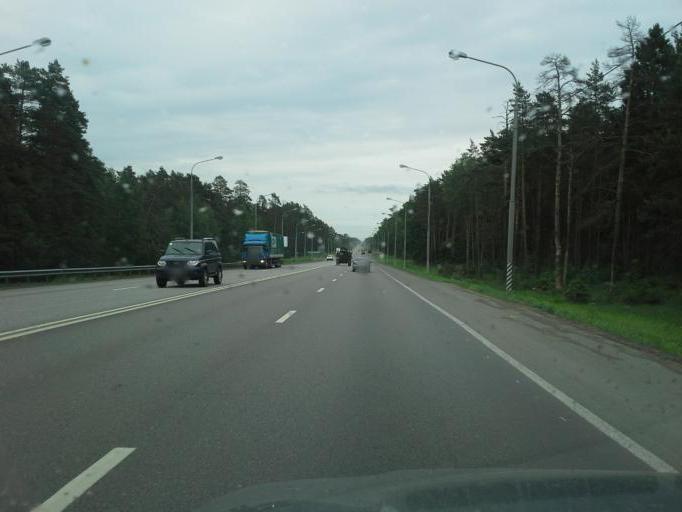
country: RU
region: Vladimir
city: Pokrov
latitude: 55.9210
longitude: 39.2168
